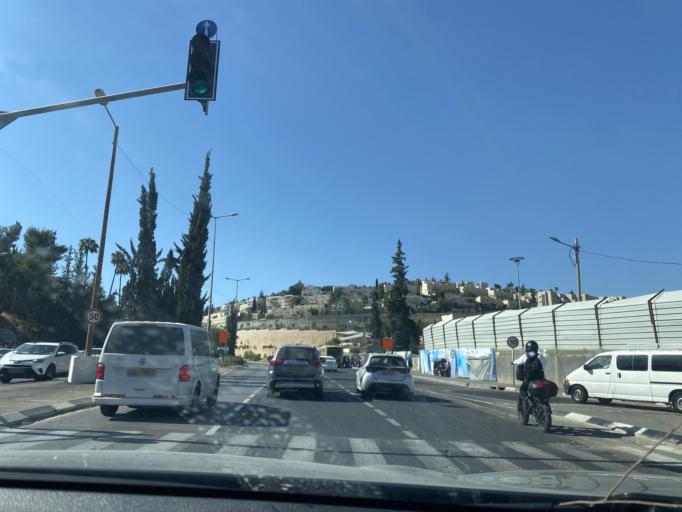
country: PS
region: West Bank
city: Bayt Iksa
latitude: 31.8090
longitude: 35.2042
